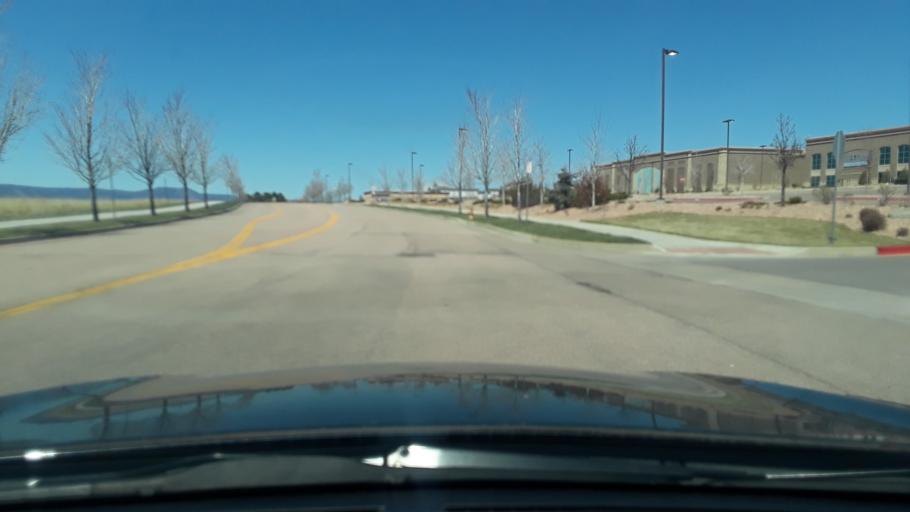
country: US
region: Colorado
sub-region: El Paso County
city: Black Forest
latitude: 38.9673
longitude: -104.7463
